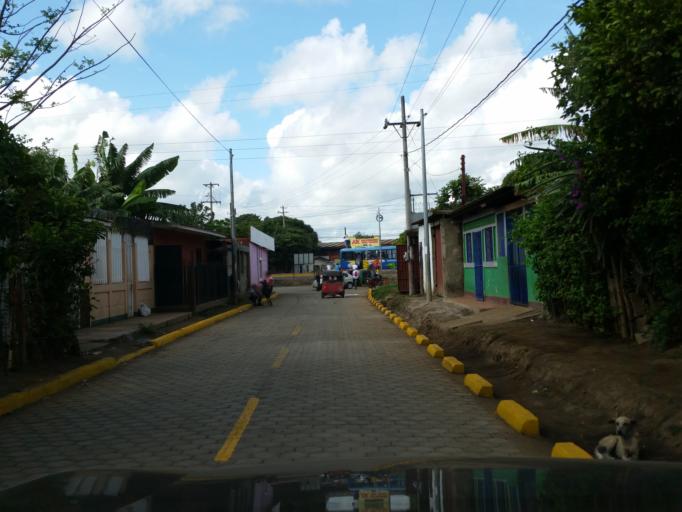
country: NI
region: Masaya
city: Masaya
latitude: 11.9871
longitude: -86.0935
